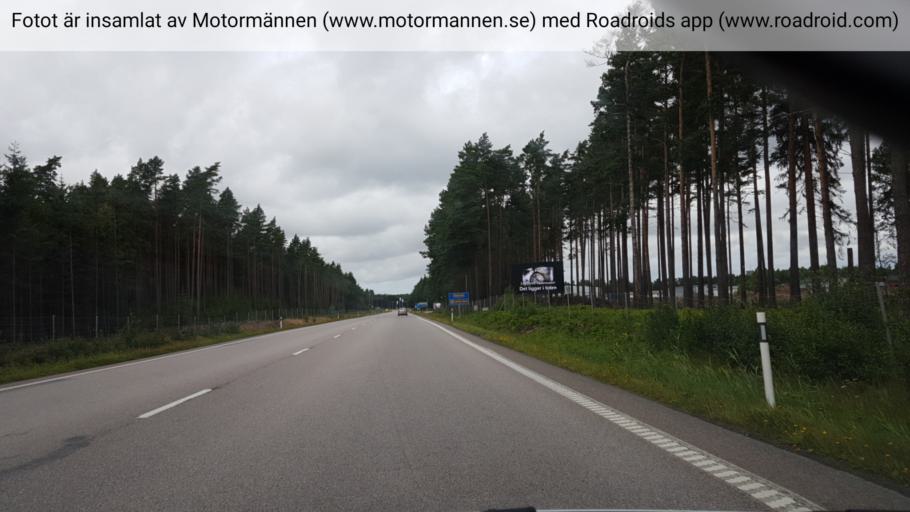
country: SE
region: Vaestra Goetaland
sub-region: Lidkopings Kommun
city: Lidkoping
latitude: 58.4833
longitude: 13.1962
